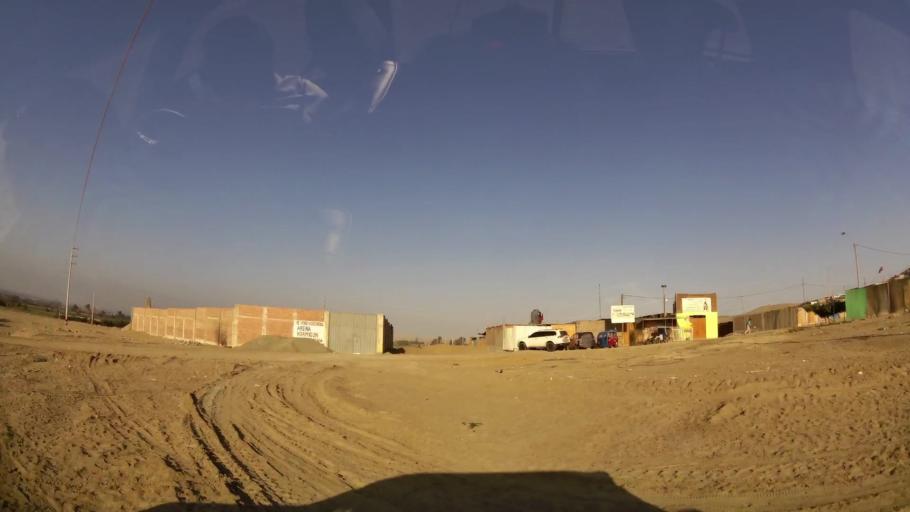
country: PE
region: Ica
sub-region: Provincia de Pisco
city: Villa Tupac Amaru
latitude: -13.7097
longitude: -76.1429
